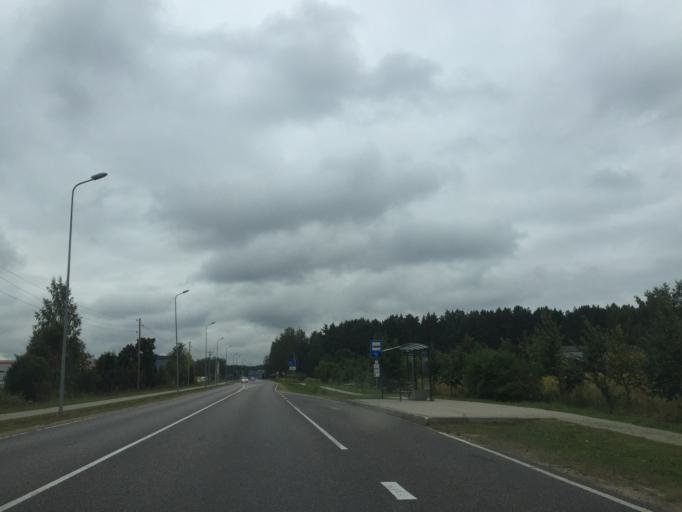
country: LV
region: Kekava
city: Balozi
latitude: 56.8962
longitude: 24.1474
